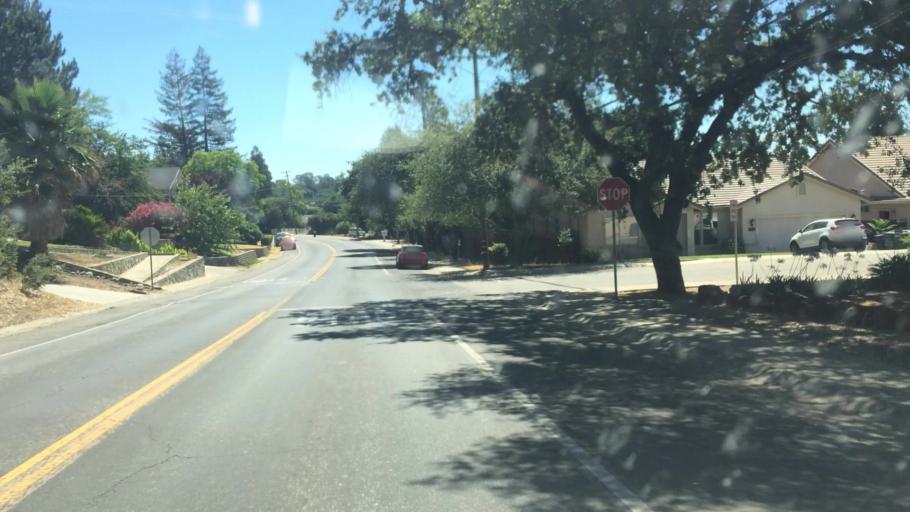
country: US
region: California
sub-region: Amador County
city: Ione
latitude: 38.3535
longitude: -120.9402
